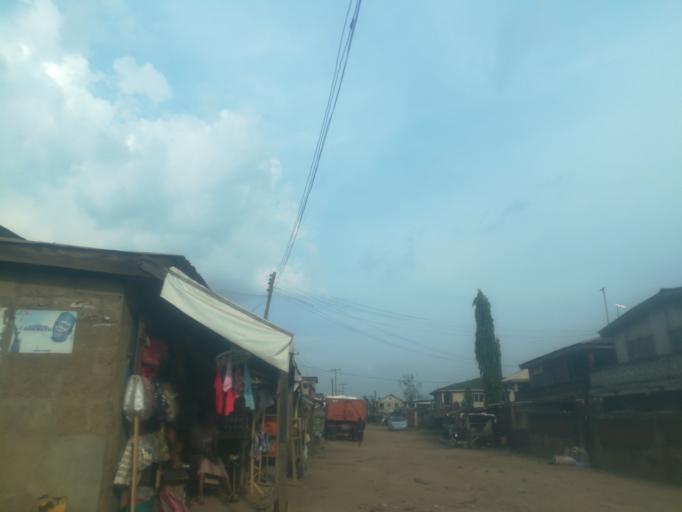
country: NG
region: Ogun
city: Abeokuta
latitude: 7.1573
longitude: 3.3109
